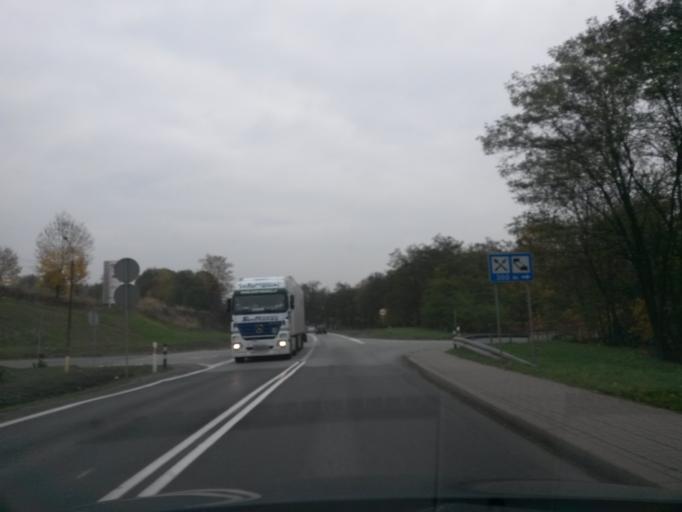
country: PL
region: Lower Silesian Voivodeship
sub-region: Powiat zabkowicki
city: Bardo
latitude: 50.5070
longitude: 16.7509
